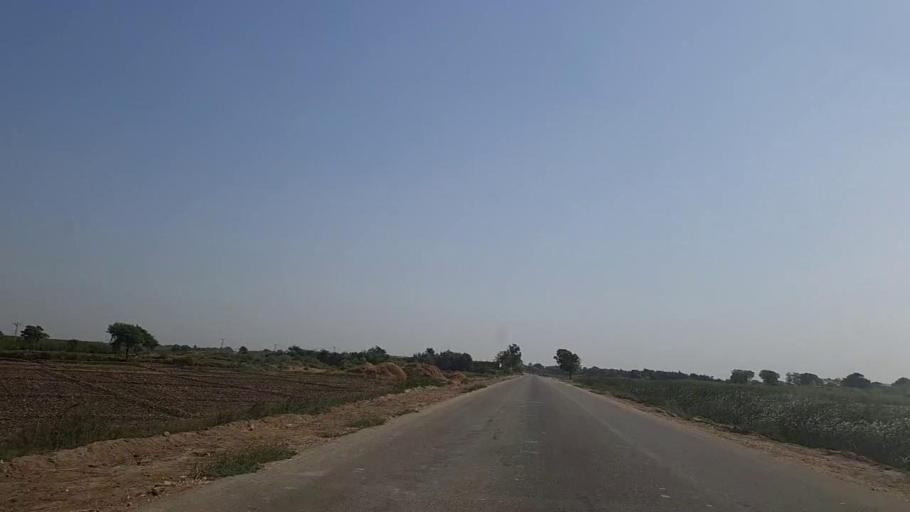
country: PK
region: Sindh
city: Daro Mehar
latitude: 24.7697
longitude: 68.2112
